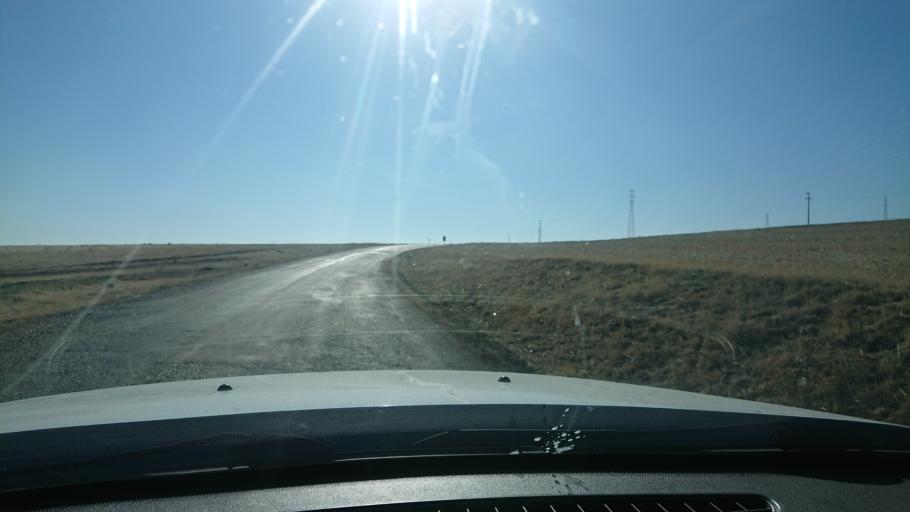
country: TR
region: Aksaray
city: Agacoren
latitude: 38.9330
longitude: 33.9191
